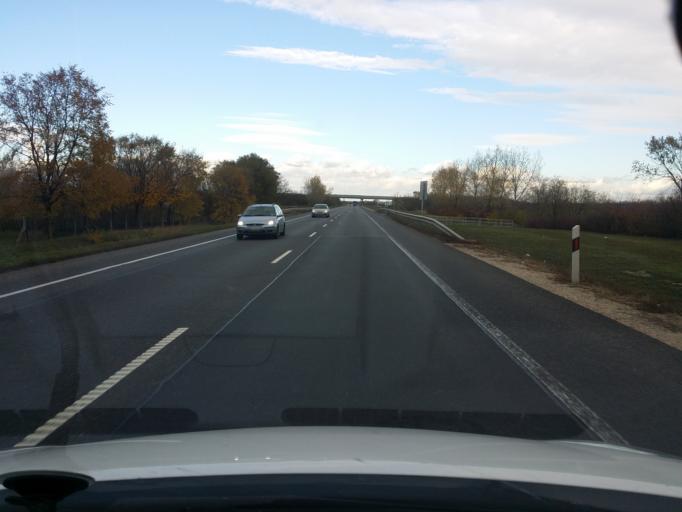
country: HU
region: Gyor-Moson-Sopron
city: Rajka
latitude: 47.9708
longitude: 17.1771
